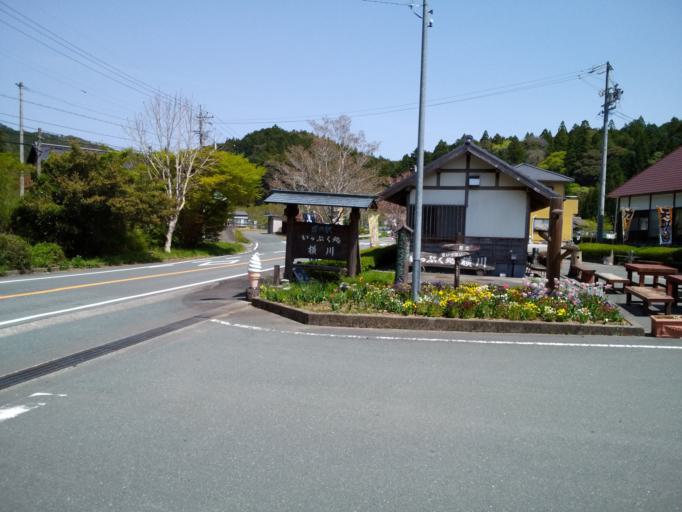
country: JP
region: Shizuoka
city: Mori
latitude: 34.9054
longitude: 137.8715
